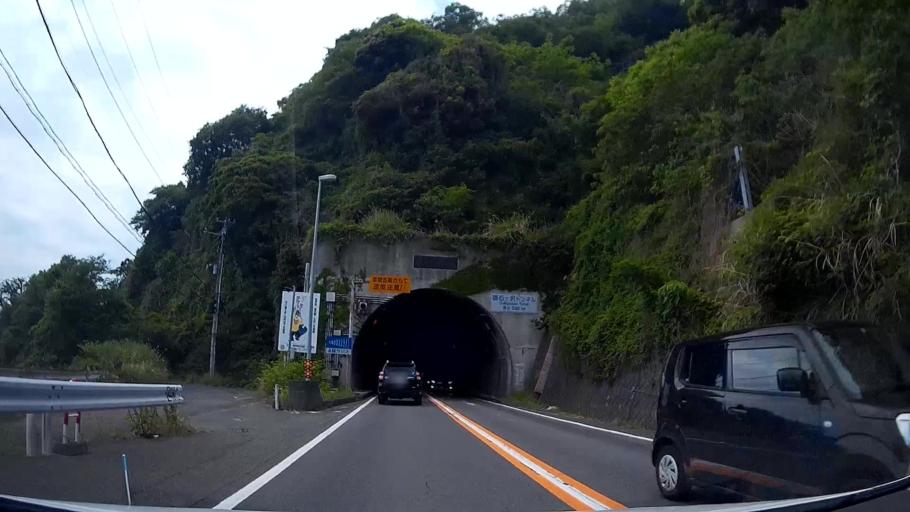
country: JP
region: Shizuoka
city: Ito
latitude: 35.0244
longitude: 139.0973
